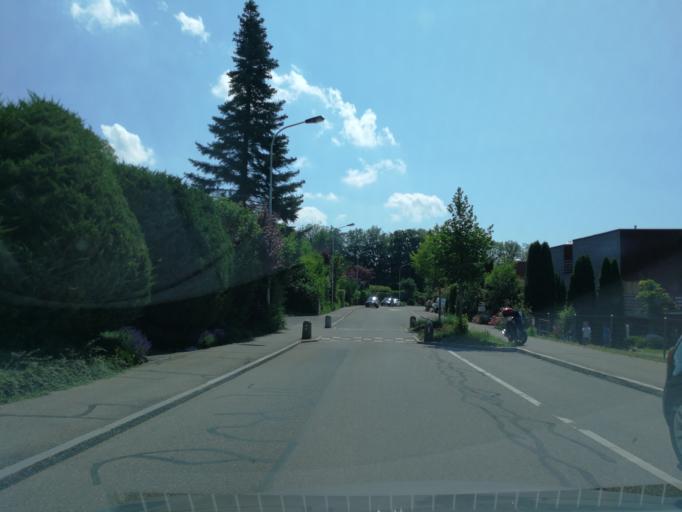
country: CH
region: Zurich
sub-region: Bezirk Meilen
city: Meilen
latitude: 47.2759
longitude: 8.6444
